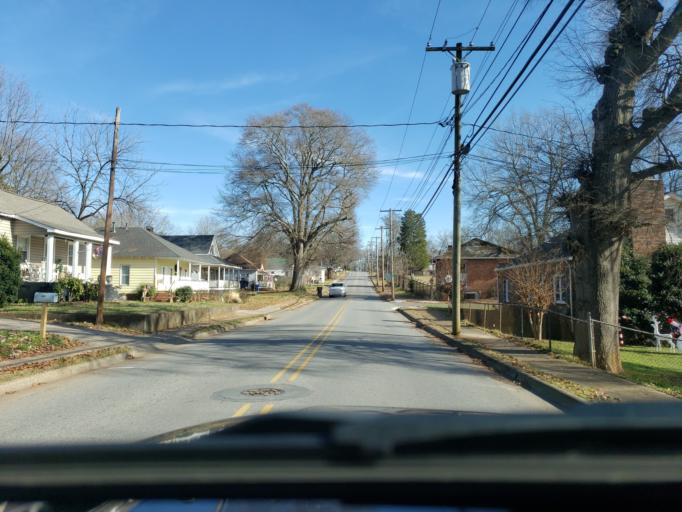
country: US
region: North Carolina
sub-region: Cleveland County
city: Kings Mountain
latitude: 35.2488
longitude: -81.3458
